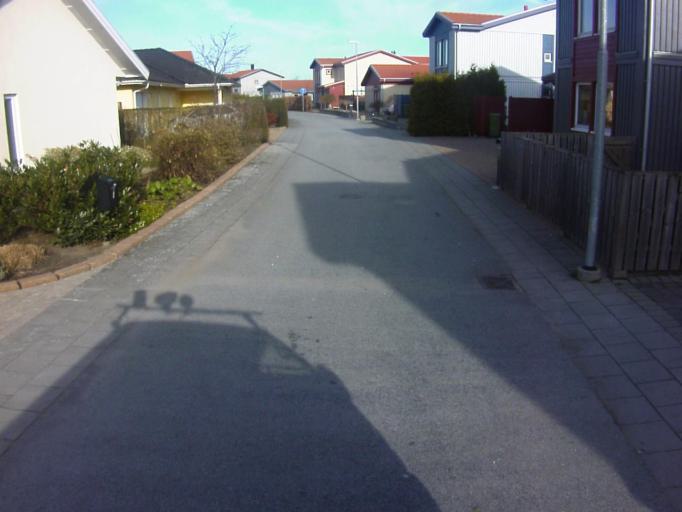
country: SE
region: Skane
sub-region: Kavlinge Kommun
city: Kaevlinge
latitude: 55.7971
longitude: 13.0960
